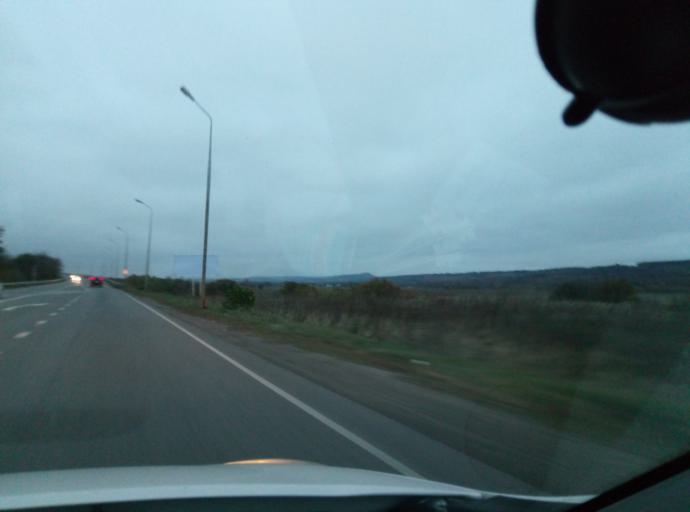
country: RU
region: Stavropol'skiy
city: Vinsady
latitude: 44.0551
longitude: 42.9475
